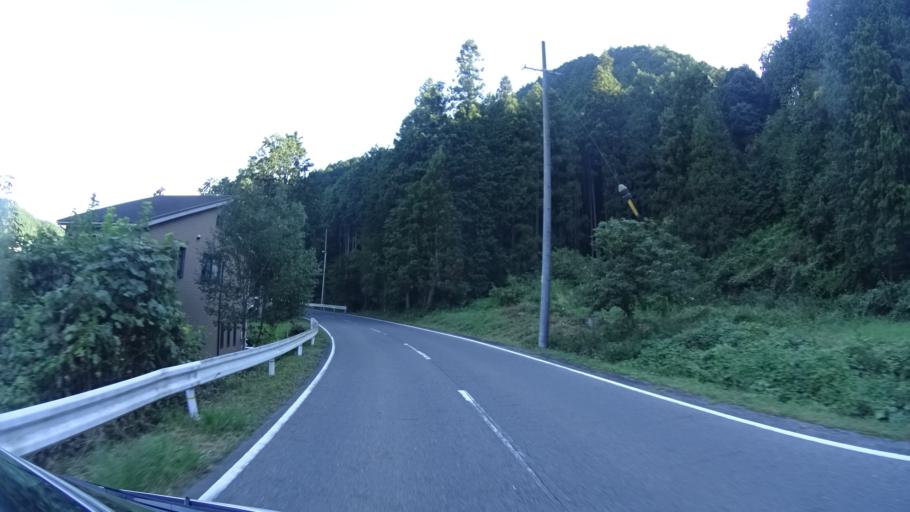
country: JP
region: Gifu
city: Minokamo
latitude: 35.5838
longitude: 137.0839
